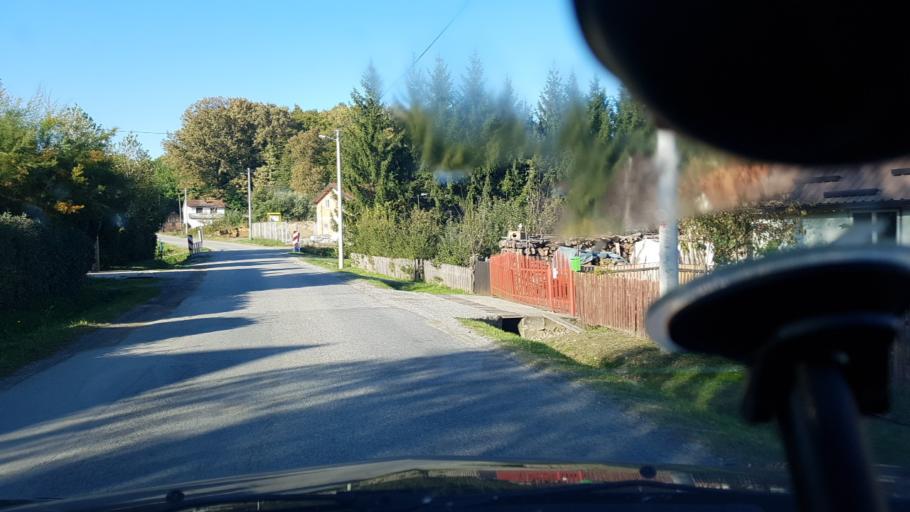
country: HR
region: Bjelovarsko-Bilogorska
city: Bjelovar
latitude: 45.9241
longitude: 16.8653
